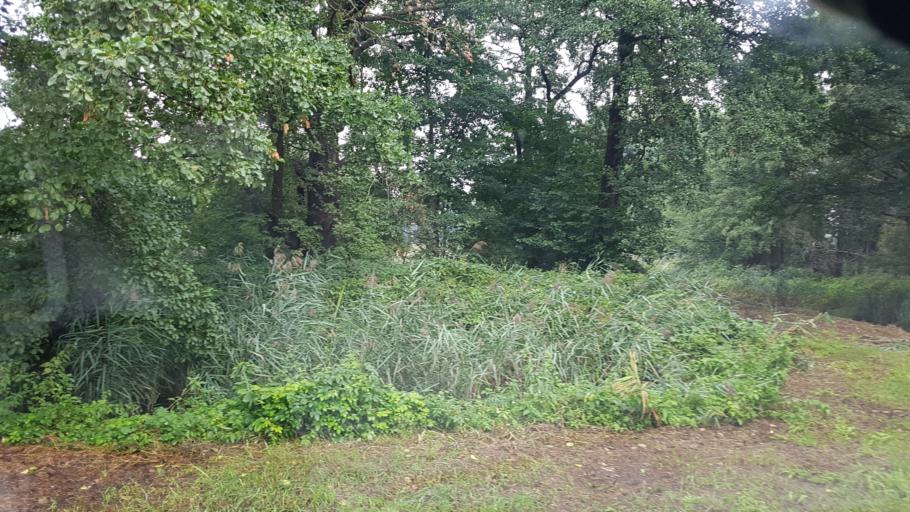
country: DE
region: Brandenburg
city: Ruckersdorf
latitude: 51.6000
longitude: 13.5641
